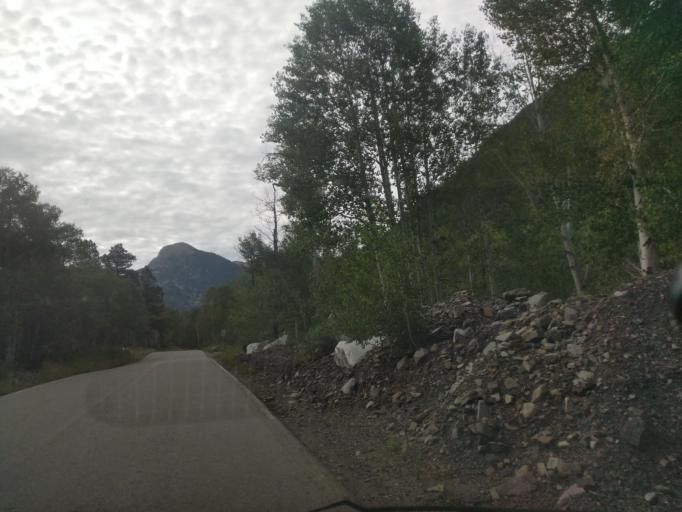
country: US
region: Colorado
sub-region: Gunnison County
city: Crested Butte
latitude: 39.0725
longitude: -107.2032
